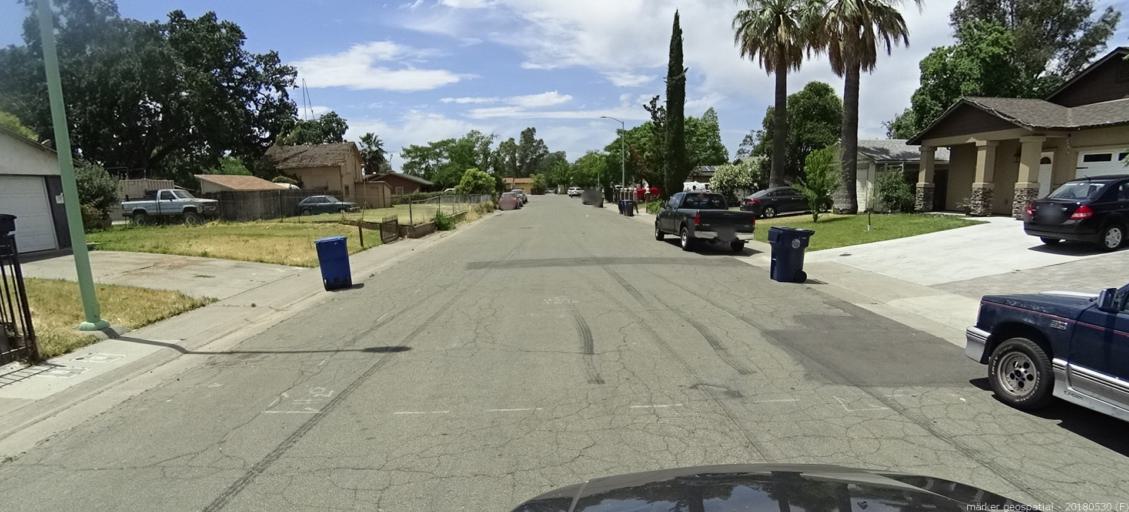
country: US
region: California
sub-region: Sacramento County
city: Sacramento
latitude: 38.6294
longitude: -121.4618
